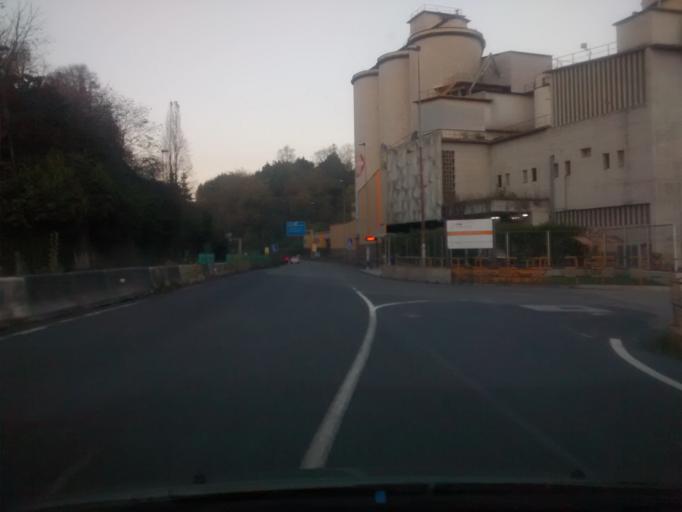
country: ES
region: Basque Country
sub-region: Provincia de Guipuzcoa
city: Lasarte
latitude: 43.2857
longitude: -1.9994
